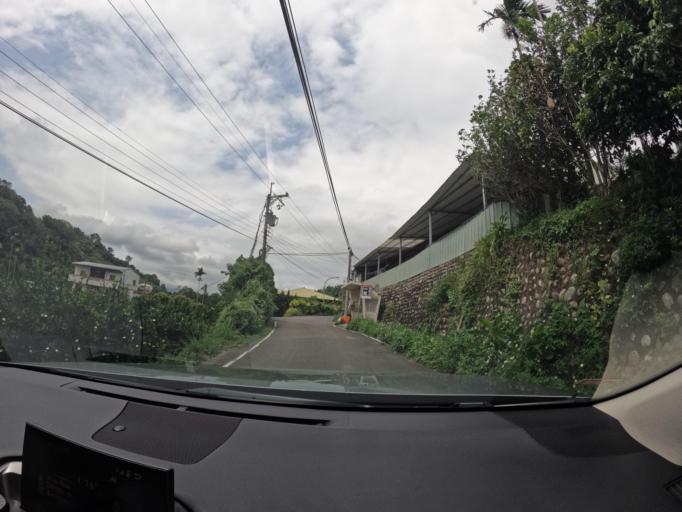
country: TW
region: Taiwan
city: Fengyuan
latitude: 24.3391
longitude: 120.8747
